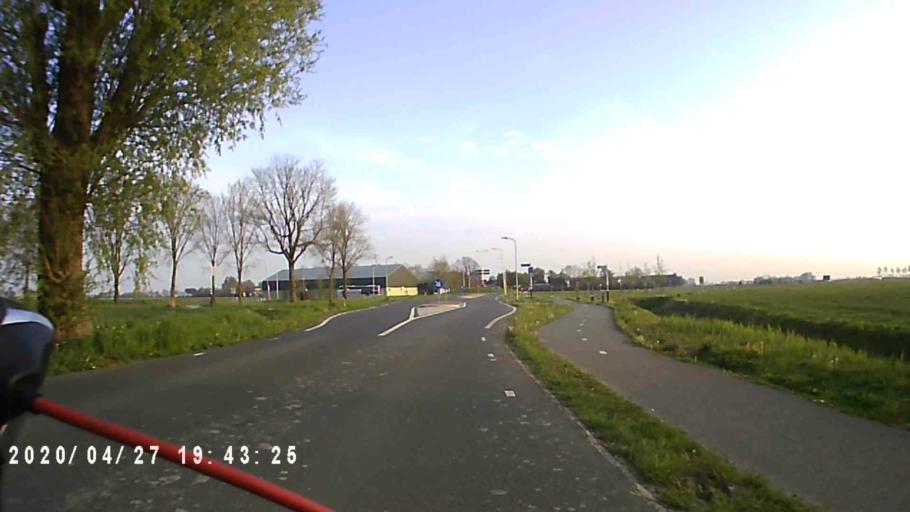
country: NL
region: Groningen
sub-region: Gemeente Winsum
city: Winsum
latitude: 53.3553
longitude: 6.4655
